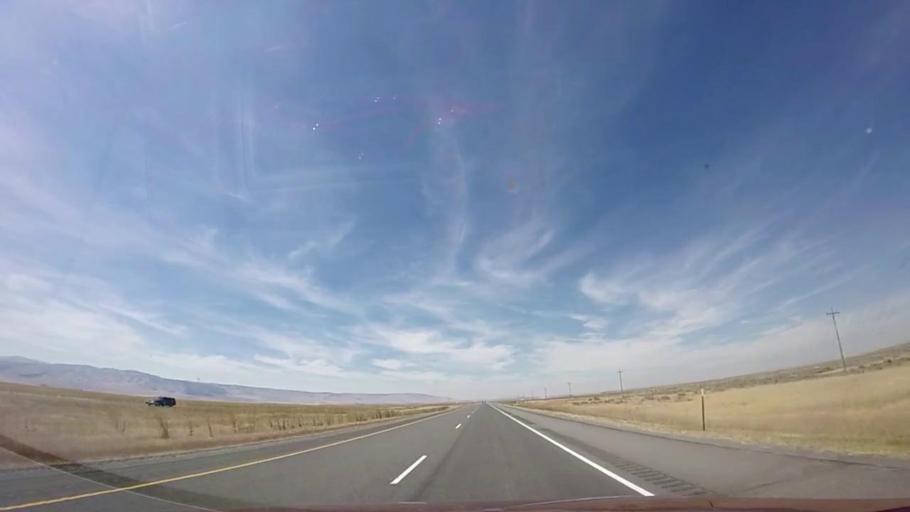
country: US
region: Idaho
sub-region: Minidoka County
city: Rupert
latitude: 42.3524
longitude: -113.2454
